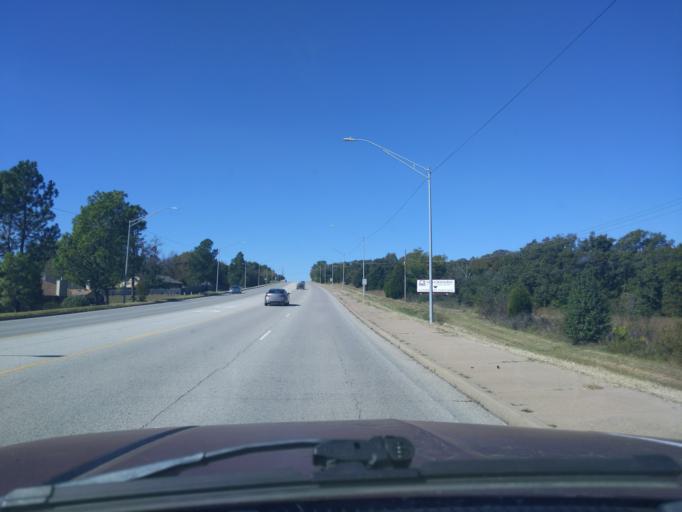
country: US
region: Oklahoma
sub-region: Creek County
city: Sapulpa
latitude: 35.9884
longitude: -96.0841
